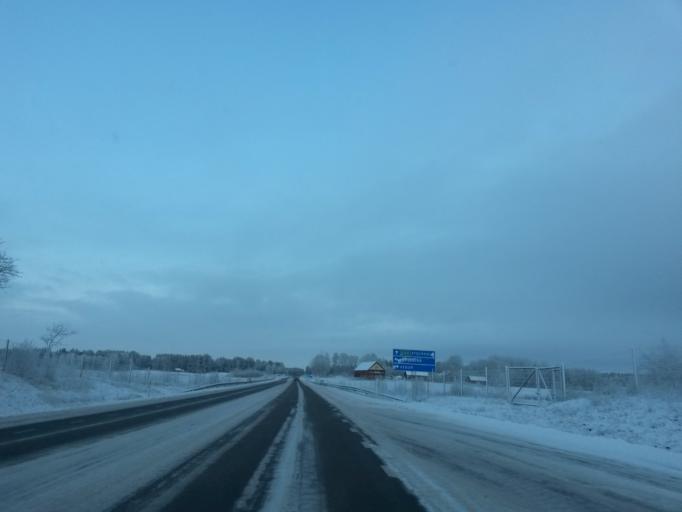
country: SE
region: Vaestra Goetaland
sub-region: Vara Kommun
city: Vara
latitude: 58.1669
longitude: 12.8866
